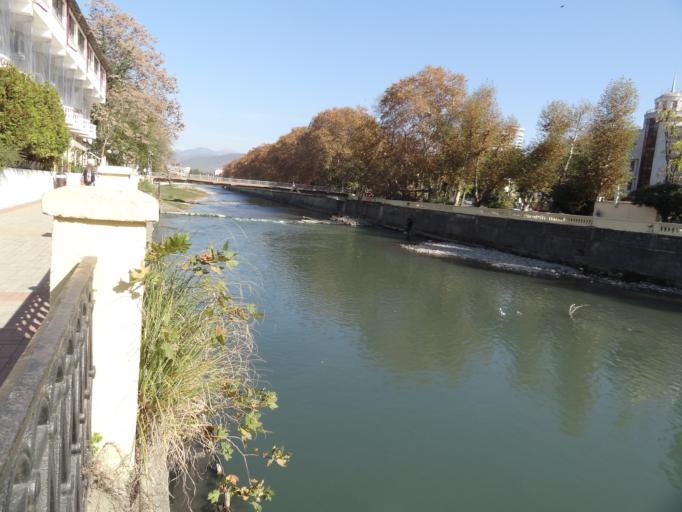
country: RU
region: Krasnodarskiy
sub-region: Sochi City
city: Sochi
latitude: 43.5873
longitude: 39.7159
